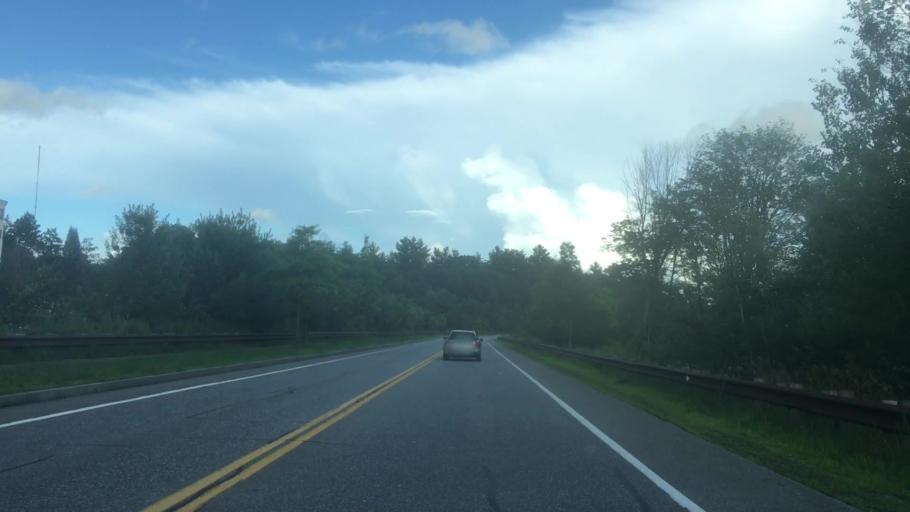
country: US
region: New Hampshire
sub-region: Merrimack County
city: Concord
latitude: 43.1938
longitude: -71.5613
